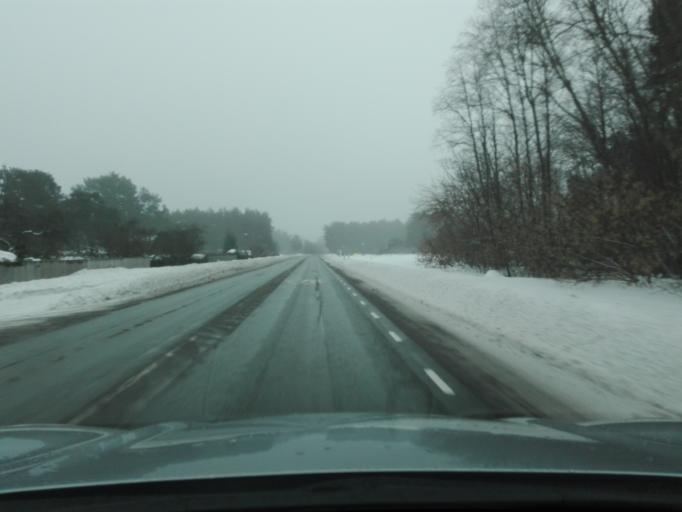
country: EE
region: Harju
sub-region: Kiili vald
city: Kiili
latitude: 59.3368
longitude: 24.7738
